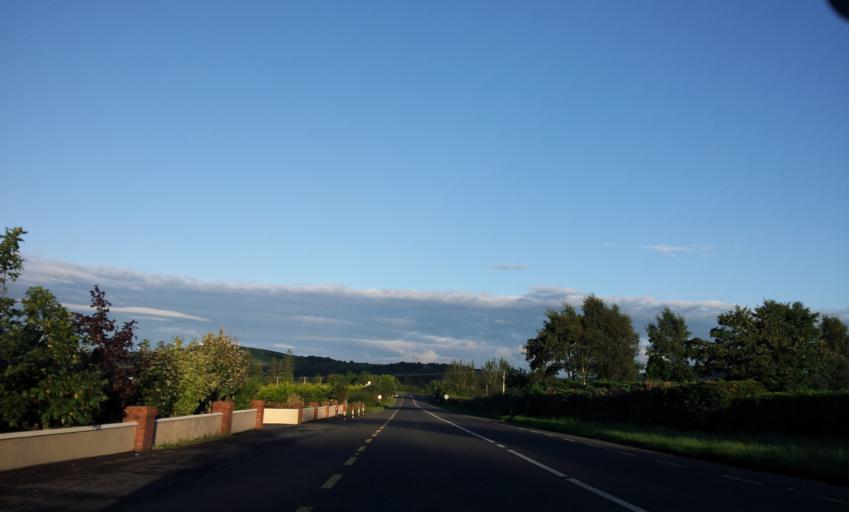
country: IE
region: Munster
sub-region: County Limerick
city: Abbeyfeale
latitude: 52.3870
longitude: -9.2376
